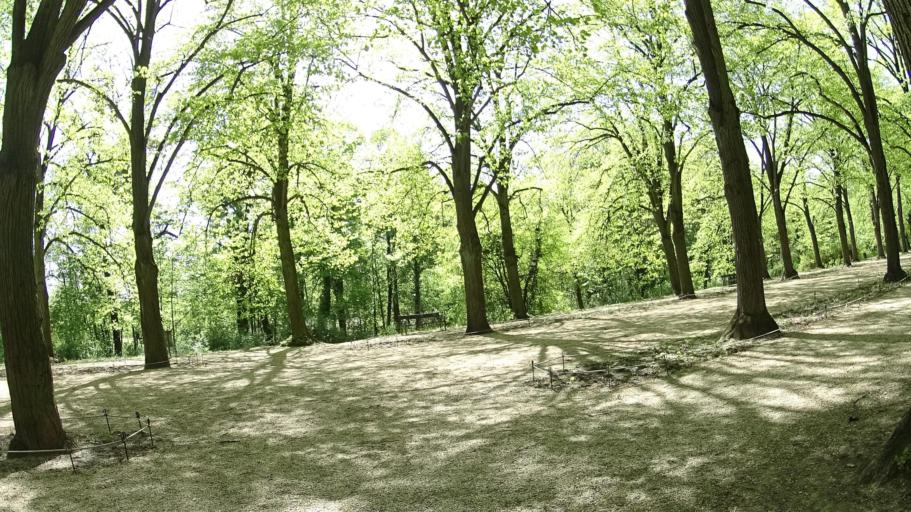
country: HU
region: Pest
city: Godollo
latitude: 47.5956
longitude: 19.3400
